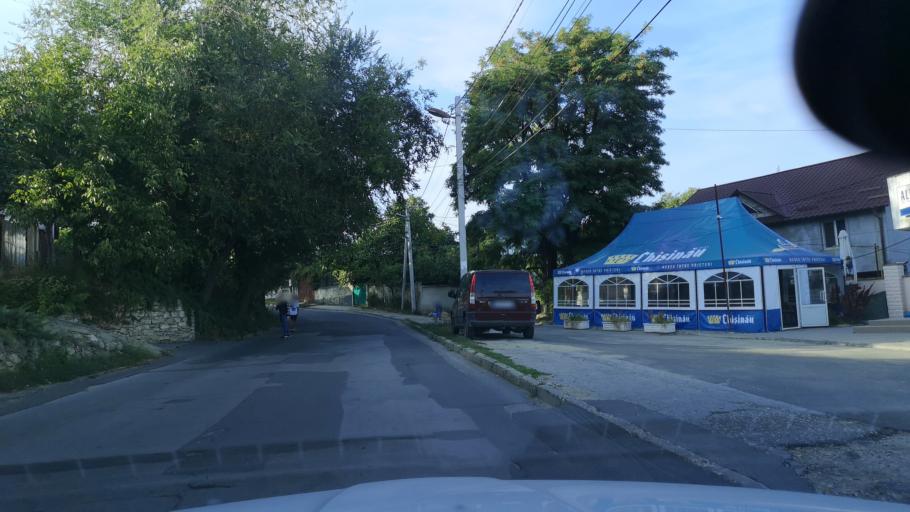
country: MD
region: Chisinau
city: Chisinau
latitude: 47.0106
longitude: 28.8478
